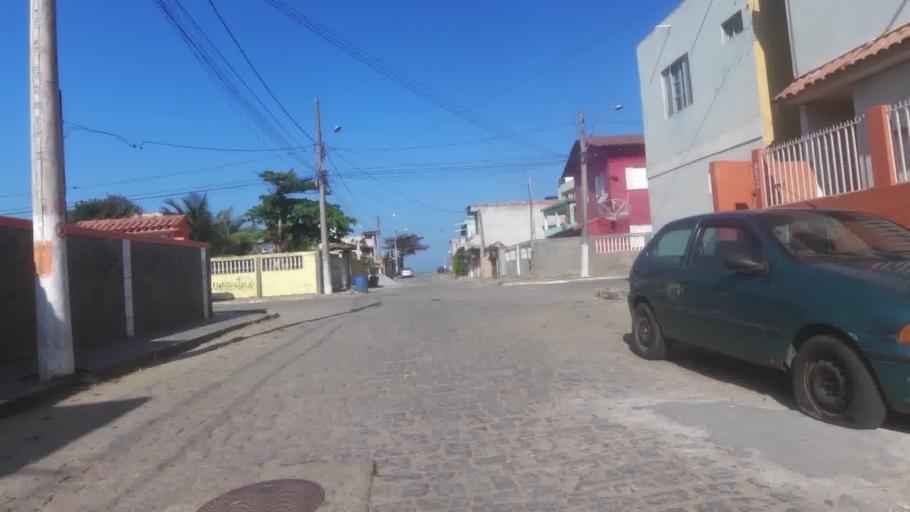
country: BR
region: Espirito Santo
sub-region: Itapemirim
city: Itapemirim
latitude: -21.0146
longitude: -40.8107
